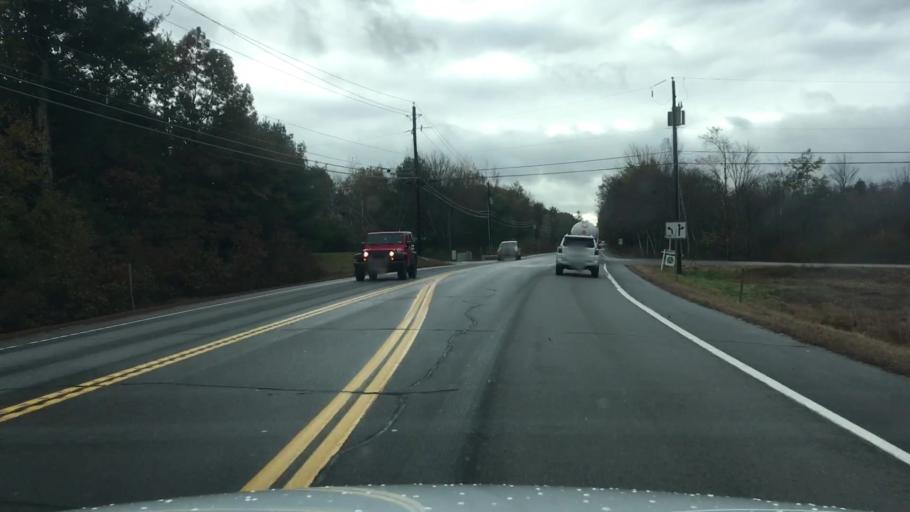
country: US
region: New Hampshire
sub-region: Strafford County
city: Lee
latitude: 43.1299
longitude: -71.0222
